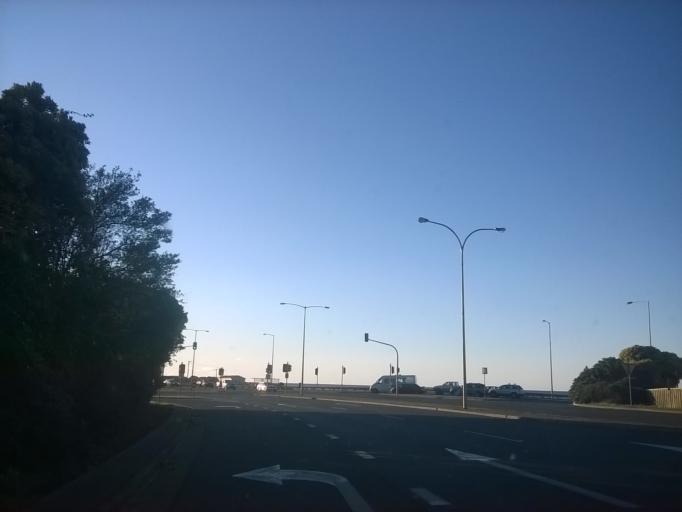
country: AU
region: Tasmania
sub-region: Burnie
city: Burnie
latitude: -41.0488
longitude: 145.9020
